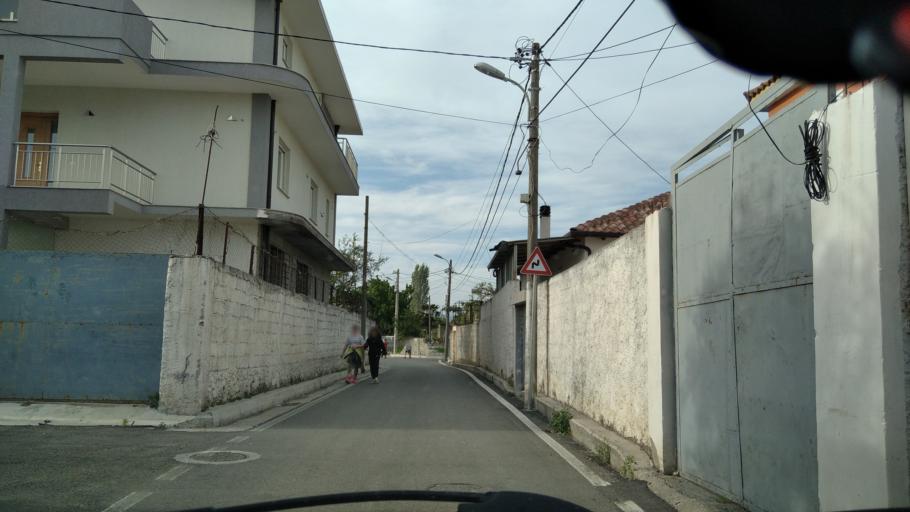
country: AL
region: Shkoder
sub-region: Rrethi i Shkodres
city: Shkoder
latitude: 42.0795
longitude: 19.5012
